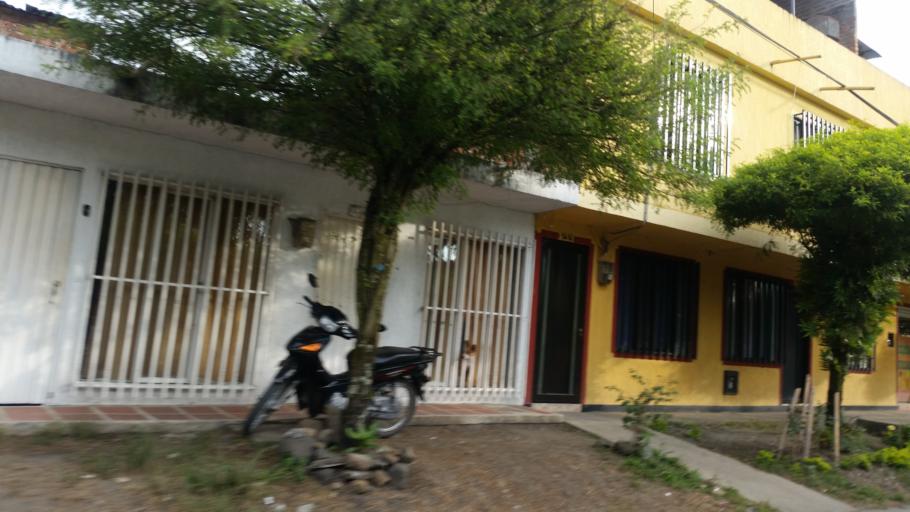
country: CO
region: Valle del Cauca
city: Ginebra
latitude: 3.7282
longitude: -76.2633
